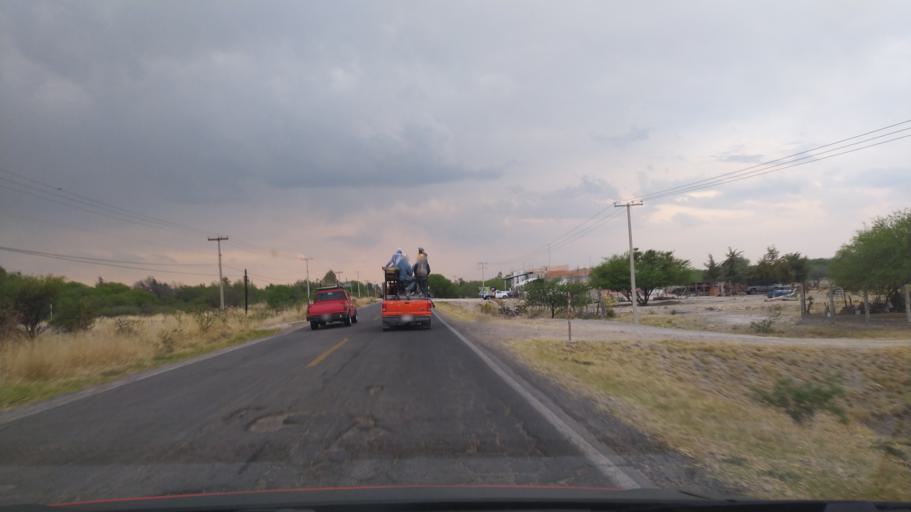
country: MX
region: Guanajuato
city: Ciudad Manuel Doblado
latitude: 20.8077
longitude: -101.9047
